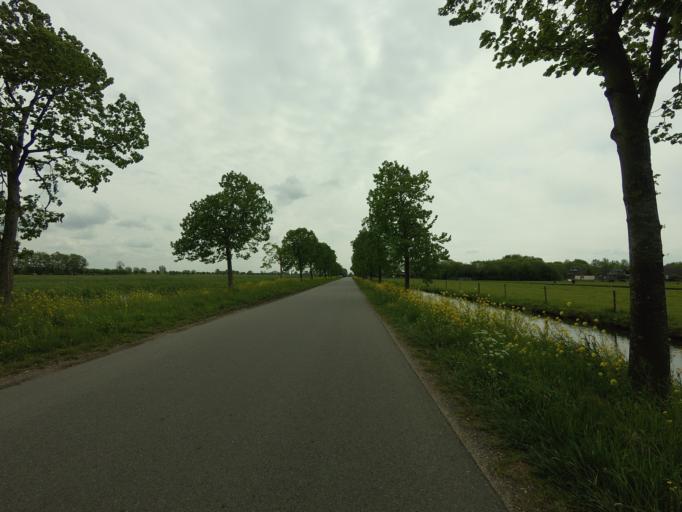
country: NL
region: Utrecht
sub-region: Gemeente Oudewater
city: Oudewater
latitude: 52.0152
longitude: 4.8758
